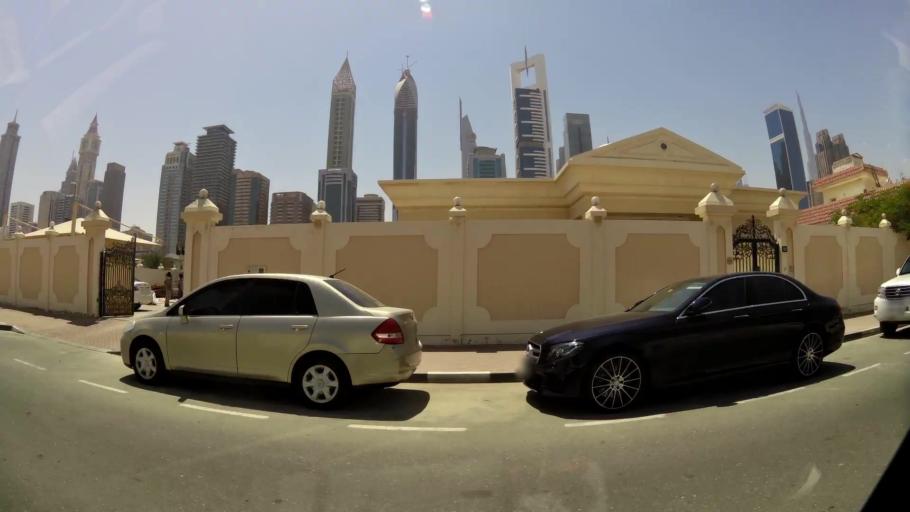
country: AE
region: Dubai
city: Dubai
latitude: 25.2141
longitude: 55.2713
